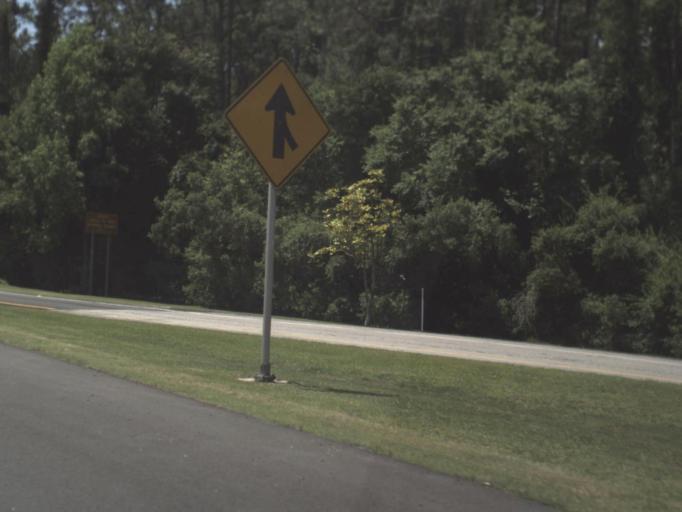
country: US
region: Florida
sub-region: Nassau County
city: Yulee
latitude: 30.6952
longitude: -81.6767
